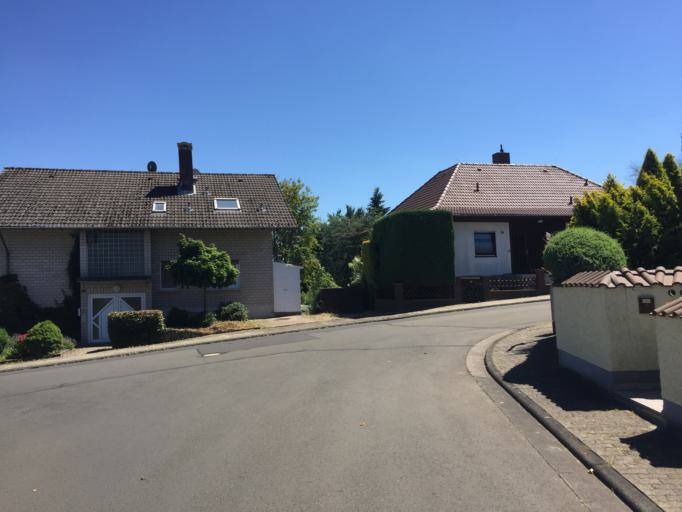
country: DE
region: Hesse
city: Beuern
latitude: 50.6249
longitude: 8.8146
